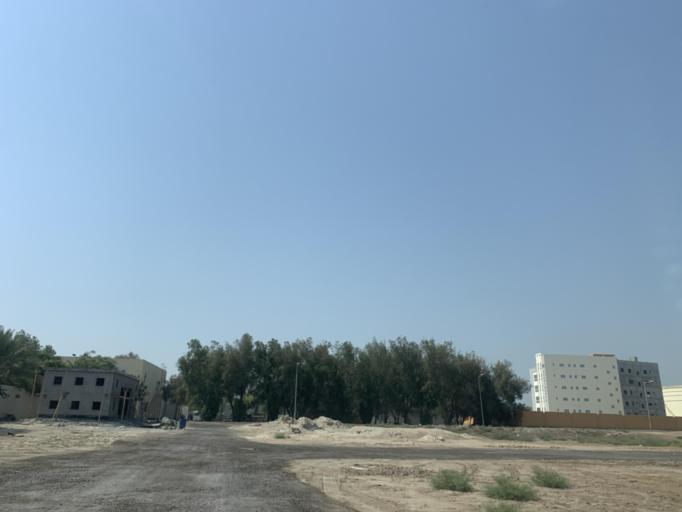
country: BH
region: Manama
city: Jidd Hafs
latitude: 26.2060
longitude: 50.5237
